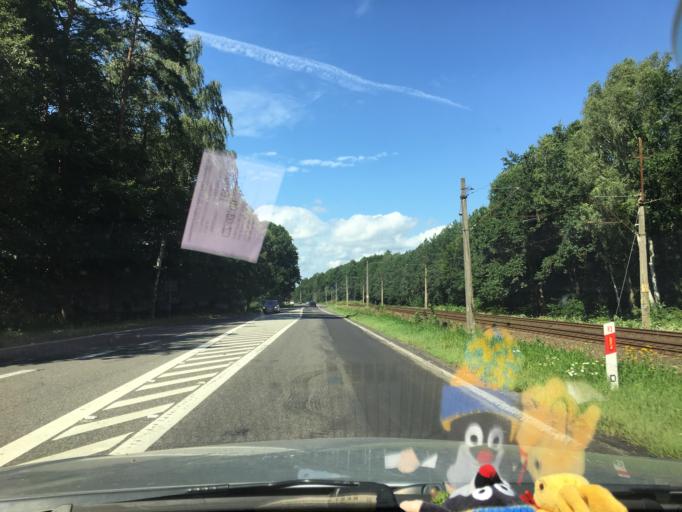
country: PL
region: West Pomeranian Voivodeship
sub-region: Powiat kamienski
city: Wolin
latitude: 53.8459
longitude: 14.6957
